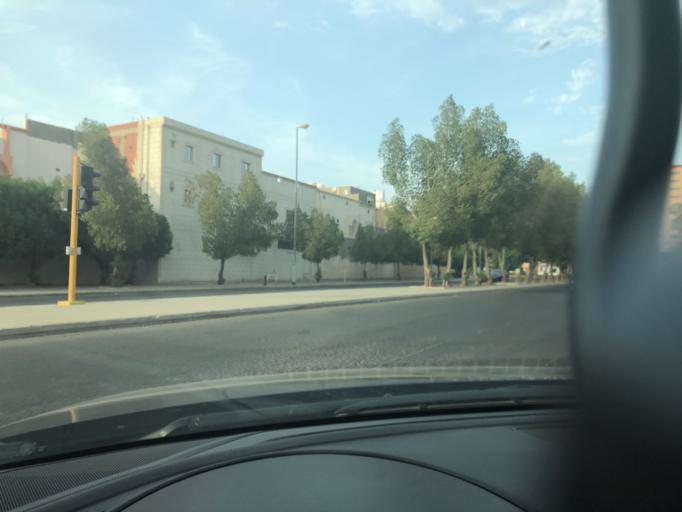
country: SA
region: Makkah
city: Mecca
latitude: 21.4103
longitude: 39.7803
